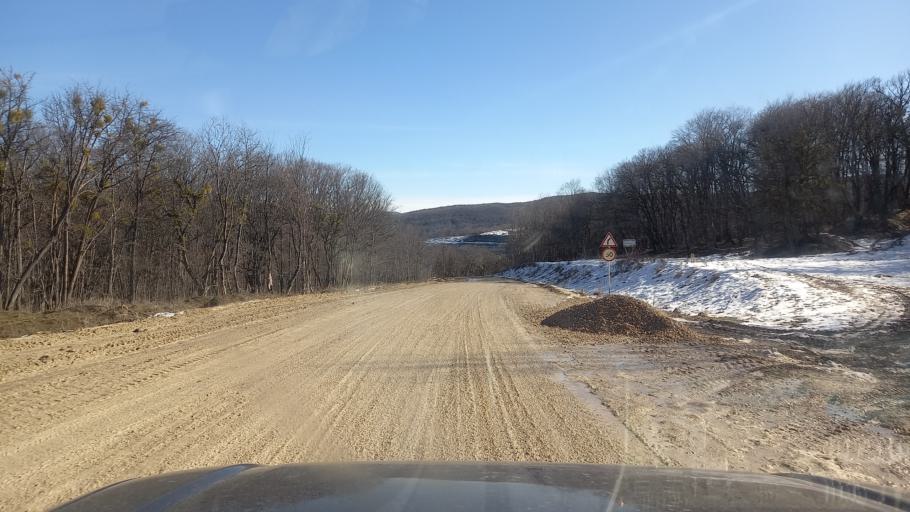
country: RU
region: Adygeya
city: Kamennomostskiy
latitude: 44.2820
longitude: 40.3210
